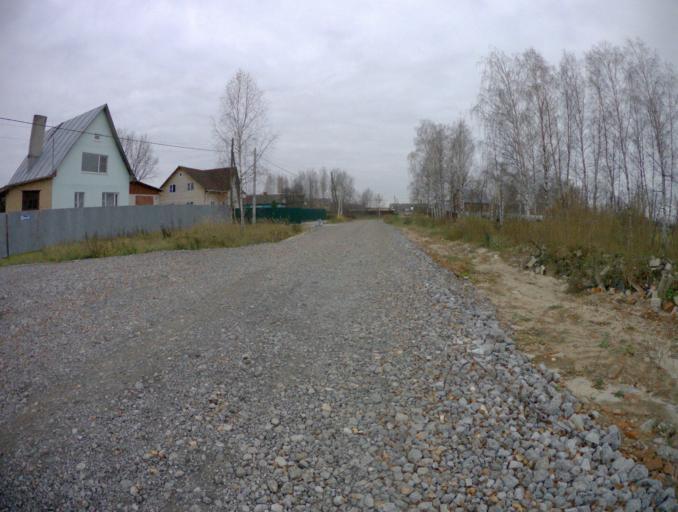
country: RU
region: Moskovskaya
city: Malaya Dubna
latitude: 55.9905
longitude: 38.9742
